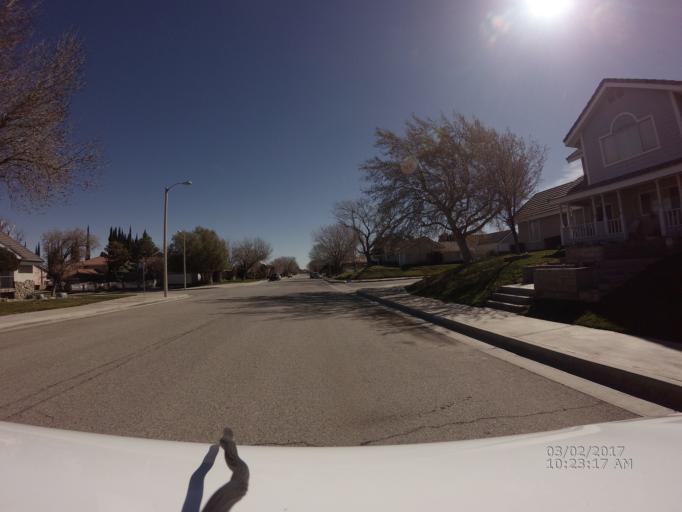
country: US
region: California
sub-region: Los Angeles County
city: Quartz Hill
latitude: 34.6402
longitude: -118.2348
